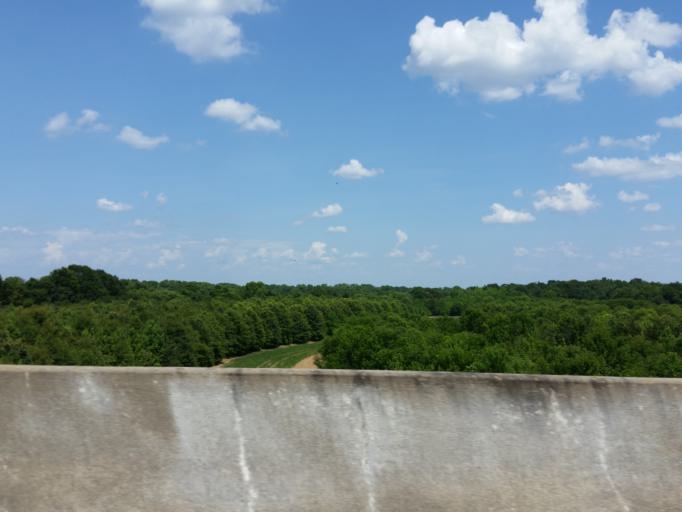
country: US
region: Alabama
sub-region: Marengo County
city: Demopolis
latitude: 32.5433
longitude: -87.8358
